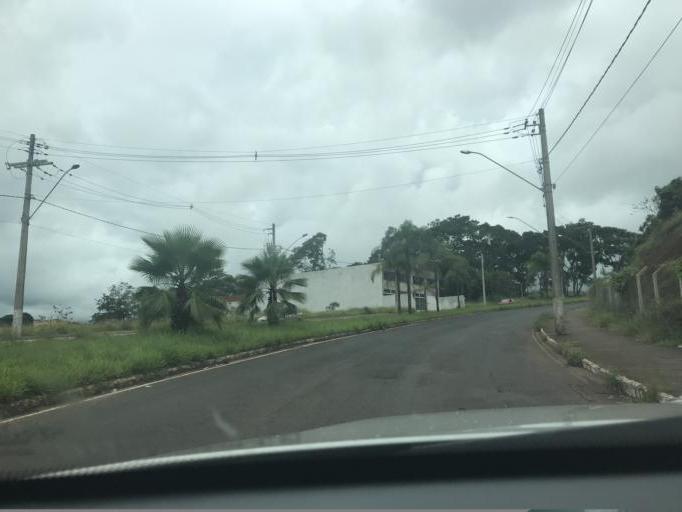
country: BR
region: Minas Gerais
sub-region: Araxa
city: Araxa
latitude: -19.5816
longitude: -46.9420
